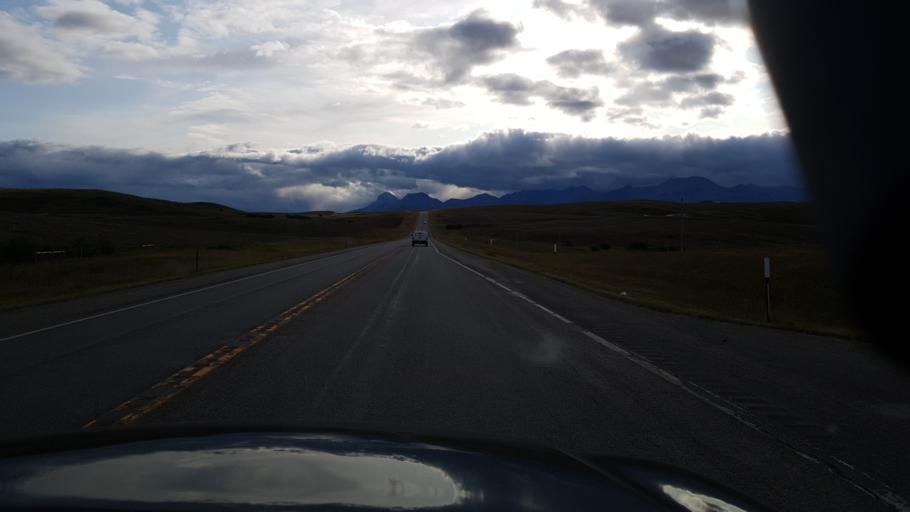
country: US
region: Montana
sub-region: Glacier County
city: South Browning
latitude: 48.5059
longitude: -113.1039
